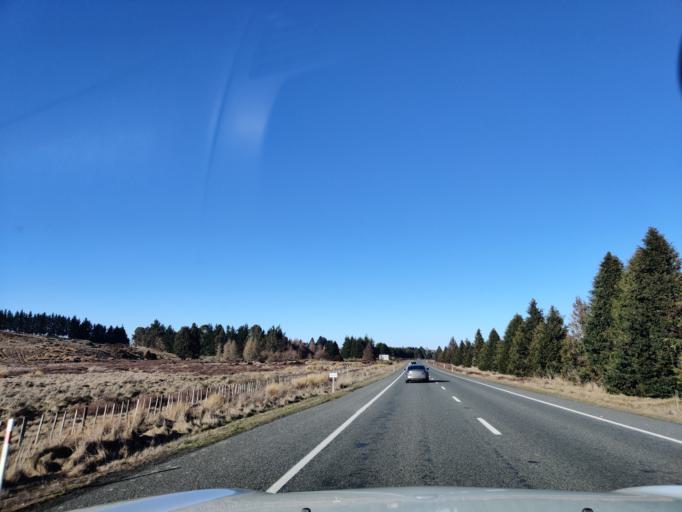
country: NZ
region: Manawatu-Wanganui
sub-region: Ruapehu District
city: Waiouru
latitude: -39.4543
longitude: 175.6771
